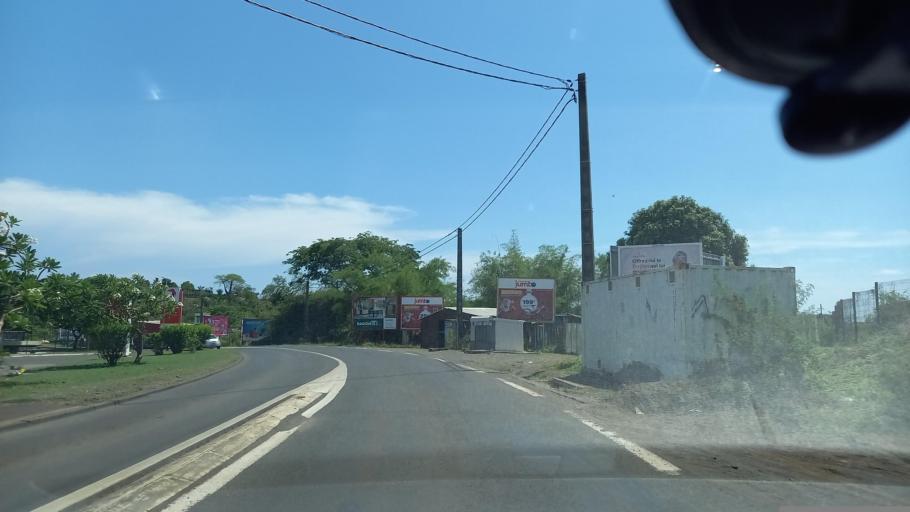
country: YT
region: Mamoudzou
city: Mamoudzou
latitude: -12.7579
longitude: 45.2323
